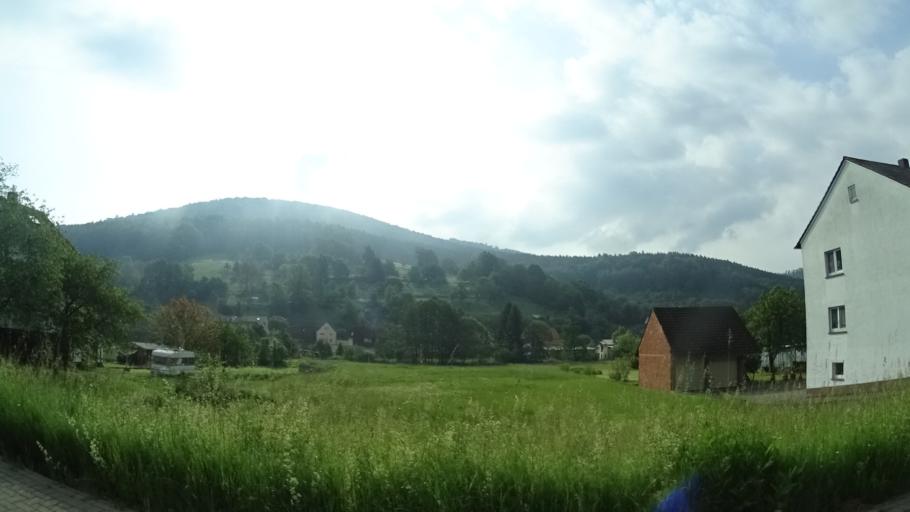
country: DE
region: Bavaria
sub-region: Regierungsbezirk Unterfranken
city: Eschau
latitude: 49.8514
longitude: 9.2756
